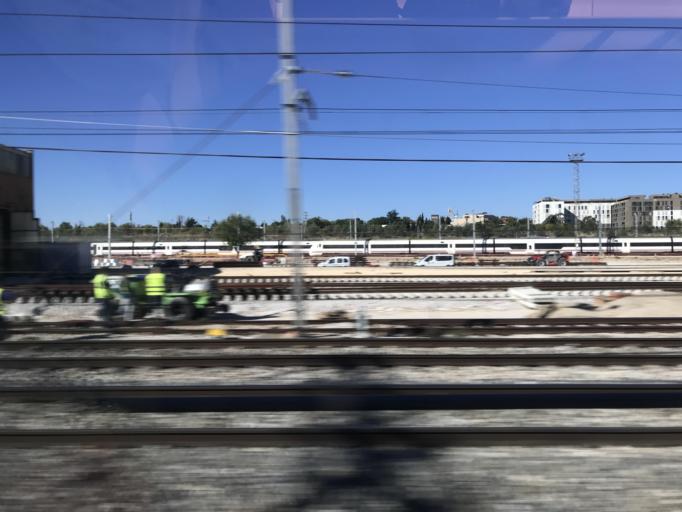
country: ES
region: Madrid
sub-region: Provincia de Madrid
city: Las Tablas
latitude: 40.5052
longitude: -3.6810
